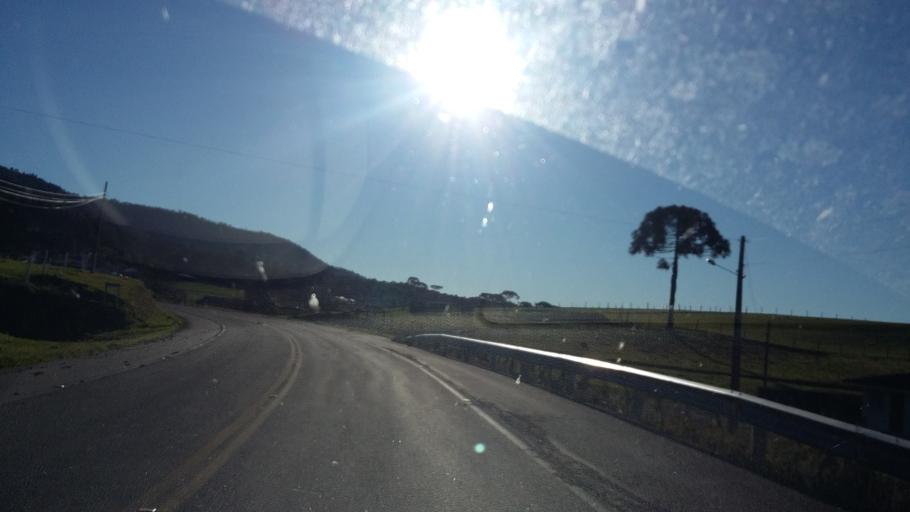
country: BR
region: Santa Catarina
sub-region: Lauro Muller
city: Lauro Muller
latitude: -28.0170
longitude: -49.5226
